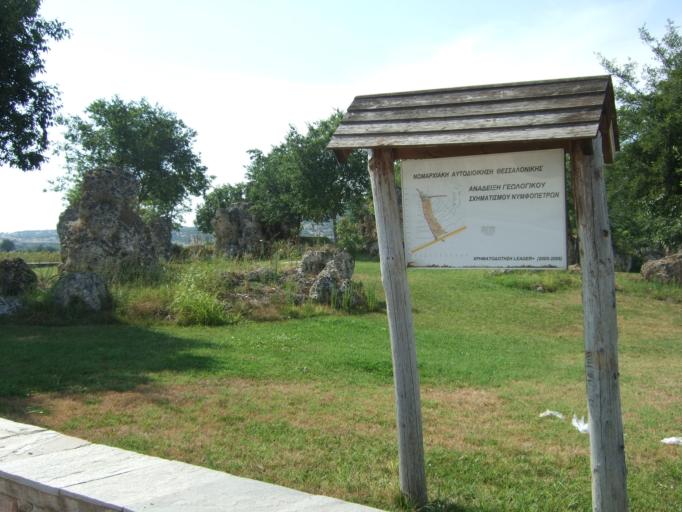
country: GR
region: Central Macedonia
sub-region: Nomos Thessalonikis
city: Askos
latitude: 40.6912
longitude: 23.3094
